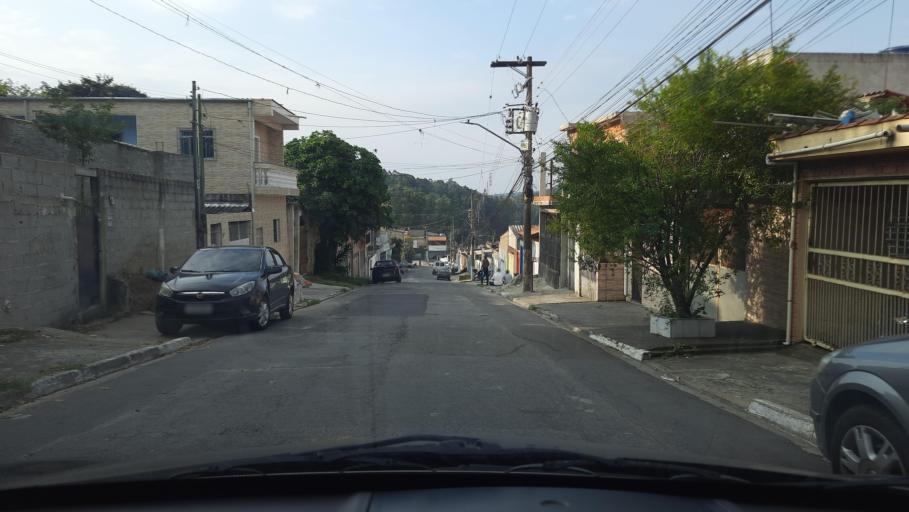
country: BR
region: Sao Paulo
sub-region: Caieiras
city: Caieiras
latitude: -23.4326
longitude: -46.7487
